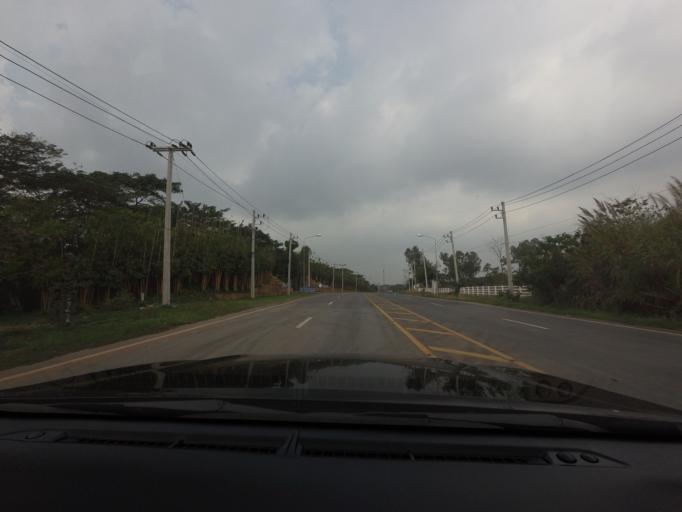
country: TH
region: Nakhon Ratchasima
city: Pak Chong
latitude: 14.5113
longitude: 101.5355
